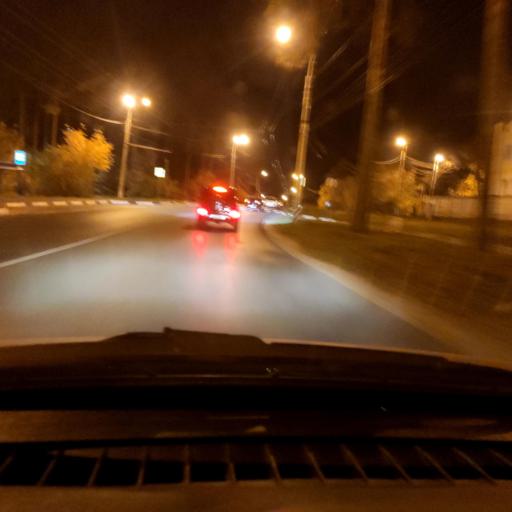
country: RU
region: Samara
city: Tol'yatti
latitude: 53.4780
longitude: 49.3590
